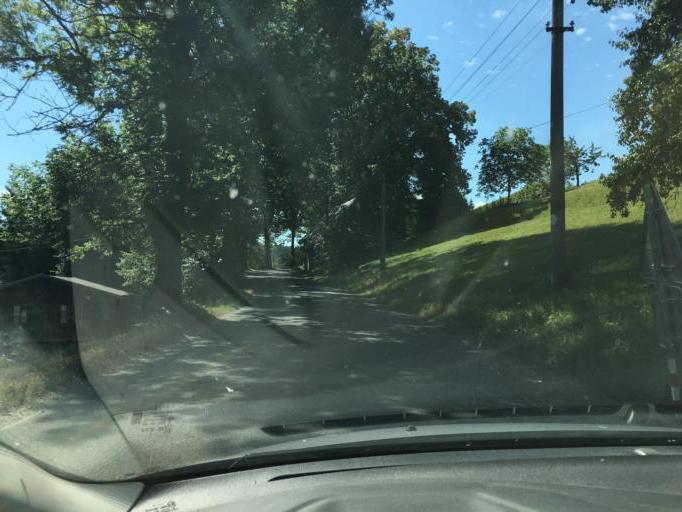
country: CZ
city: Plavy
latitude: 50.7053
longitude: 15.3530
